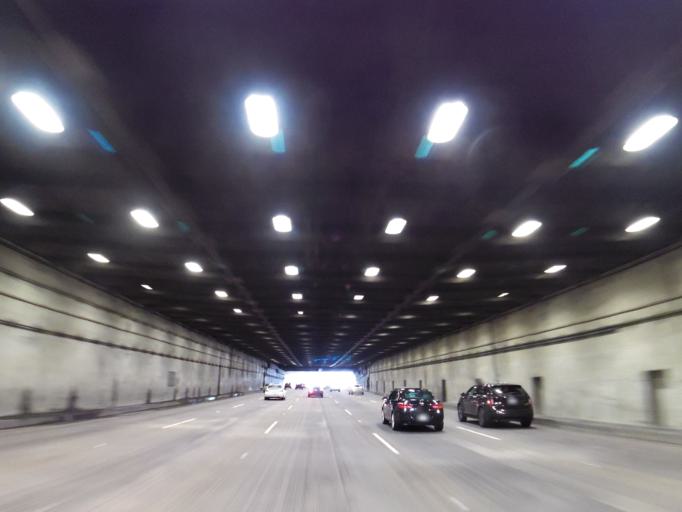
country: US
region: California
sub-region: San Francisco County
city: San Francisco
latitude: 37.8096
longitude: -122.3656
